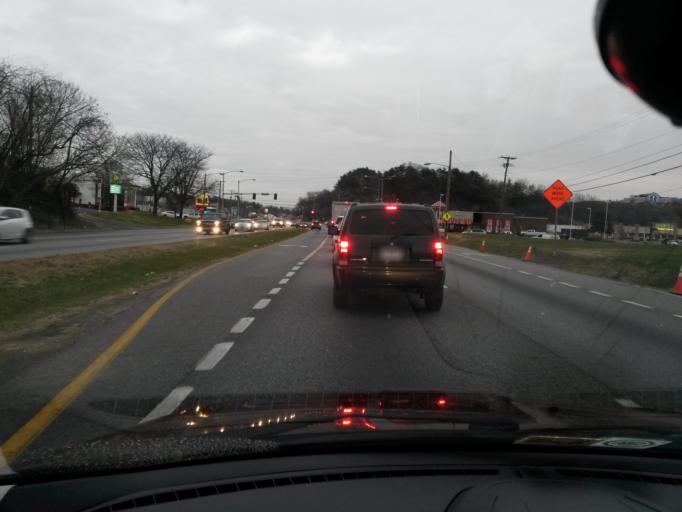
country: US
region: Virginia
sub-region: Roanoke County
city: Vinton
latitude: 37.3004
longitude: -79.8944
